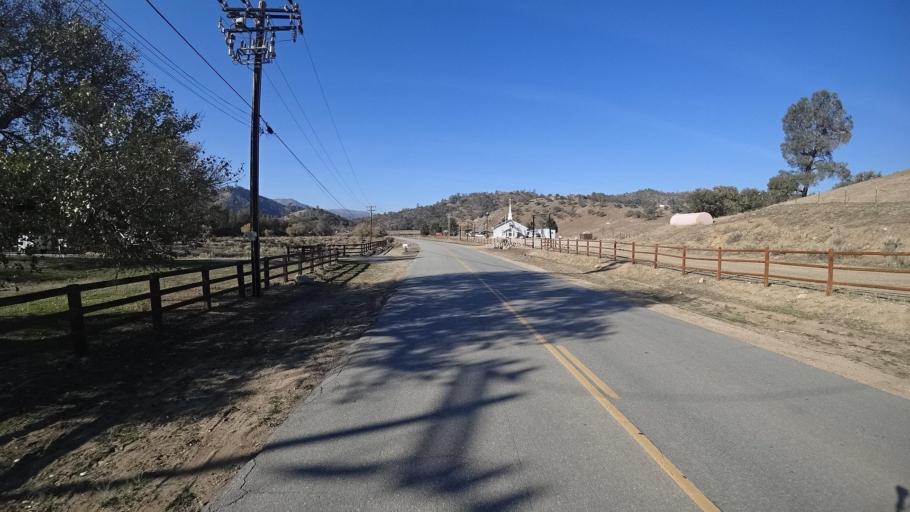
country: US
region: California
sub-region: Kern County
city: Tehachapi
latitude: 35.3119
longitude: -118.4135
